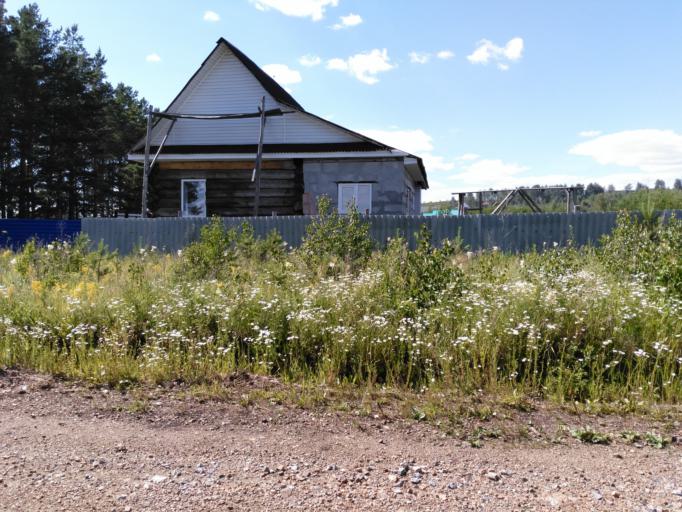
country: RU
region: Bashkortostan
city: Uchaly
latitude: 54.2870
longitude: 59.3582
